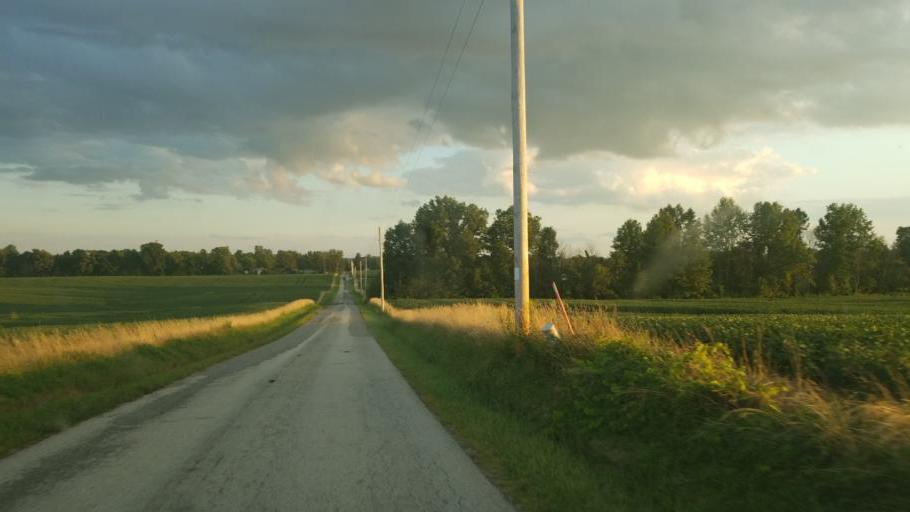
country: US
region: Ohio
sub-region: Richland County
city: Mansfield
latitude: 40.8265
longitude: -82.5424
